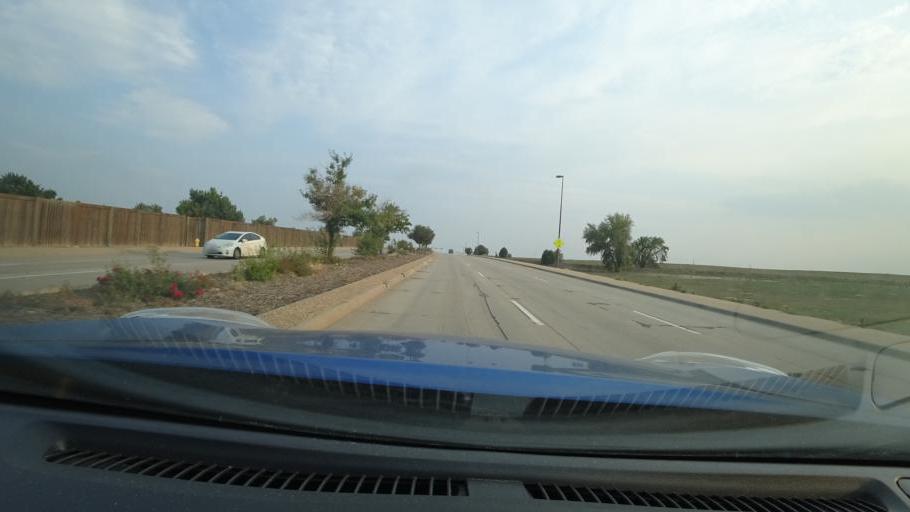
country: US
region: Colorado
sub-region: Adams County
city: Aurora
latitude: 39.7431
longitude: -104.7914
